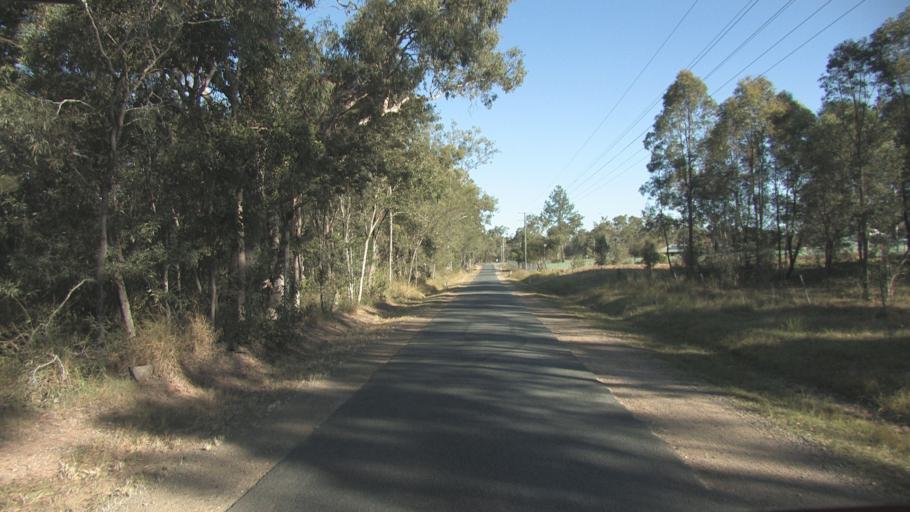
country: AU
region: Queensland
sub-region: Logan
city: North Maclean
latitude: -27.7885
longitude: 153.0384
